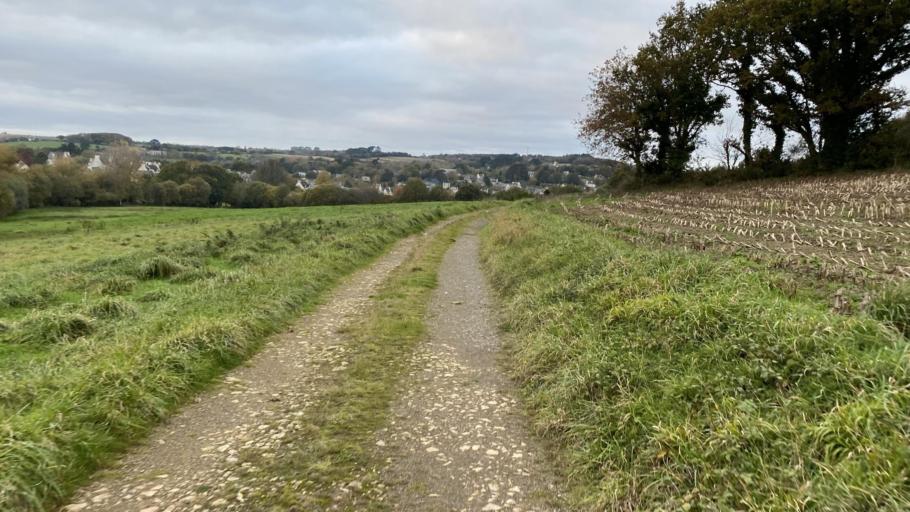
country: FR
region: Brittany
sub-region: Departement du Finistere
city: Daoulas
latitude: 48.3556
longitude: -4.2526
